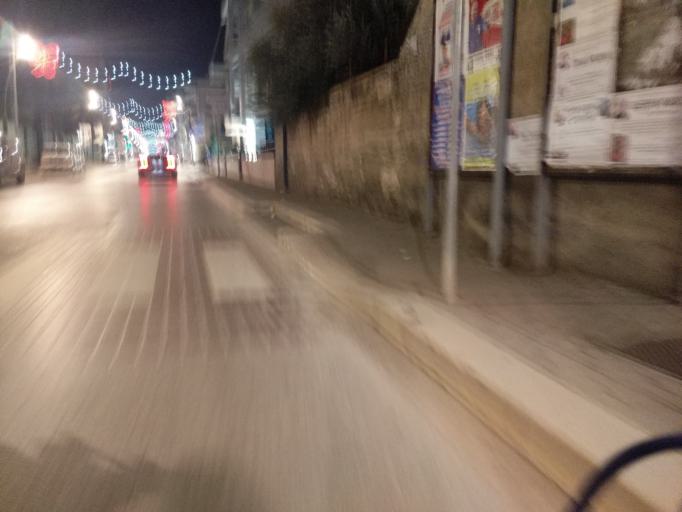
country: IT
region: Apulia
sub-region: Provincia di Bari
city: Modugno
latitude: 41.0865
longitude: 16.7871
